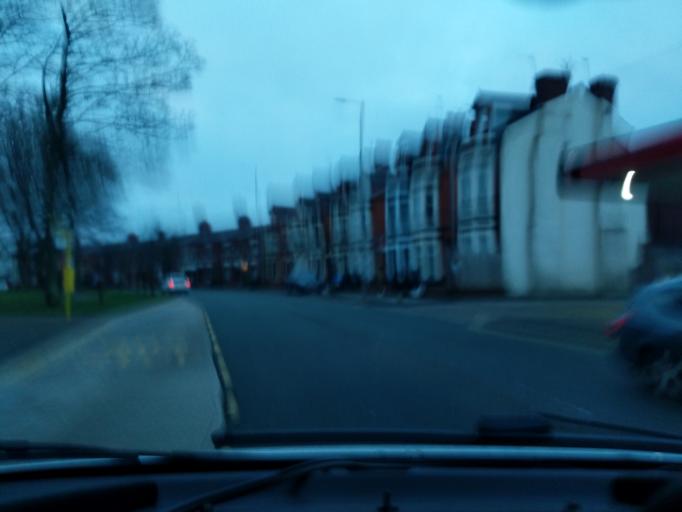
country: GB
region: England
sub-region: St. Helens
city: St Helens
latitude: 53.4676
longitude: -2.7291
